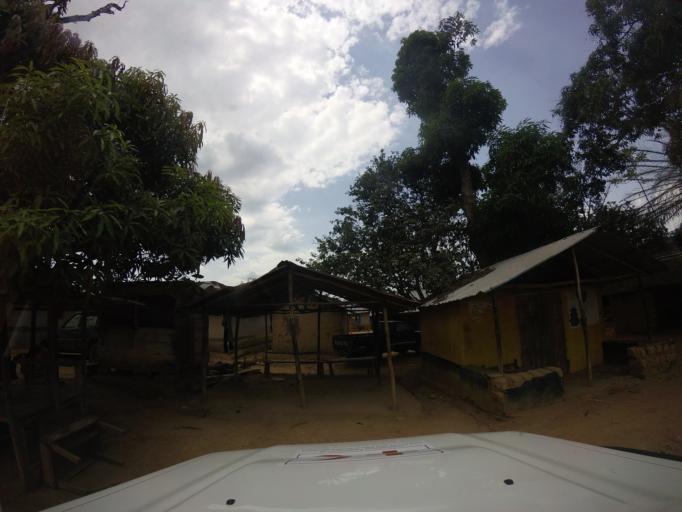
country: SL
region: Southern Province
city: Zimmi
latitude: 7.2212
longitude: -11.1757
